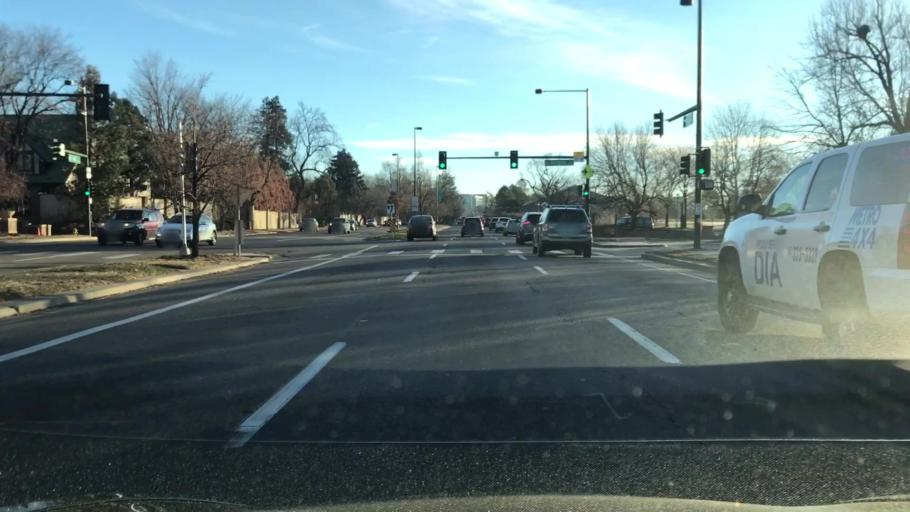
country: US
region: Colorado
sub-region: Denver County
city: Denver
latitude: 39.7182
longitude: -104.9672
